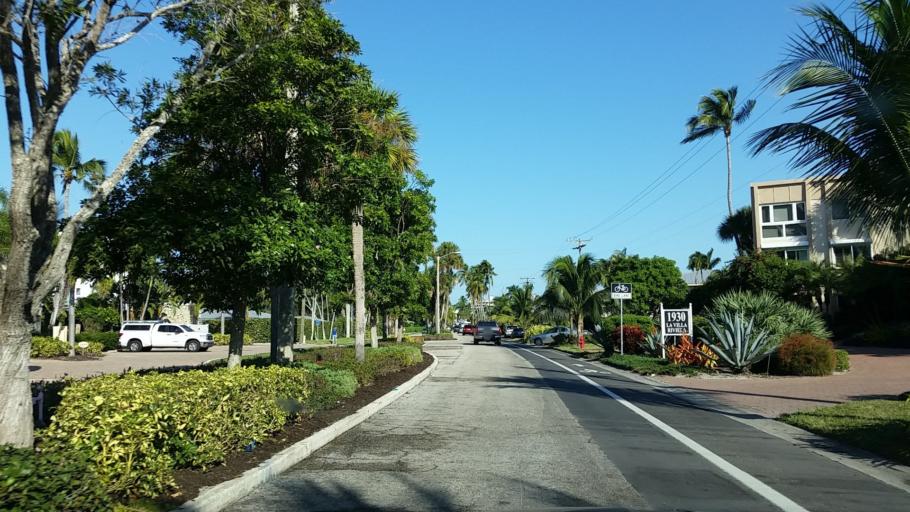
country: US
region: Florida
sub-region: Collier County
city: Naples
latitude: 26.1687
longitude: -81.8108
